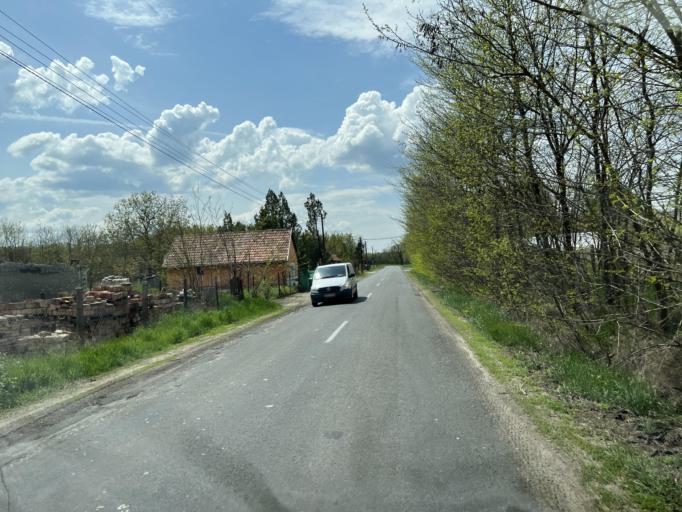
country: HU
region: Pest
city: Csemo
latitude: 47.1302
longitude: 19.7128
